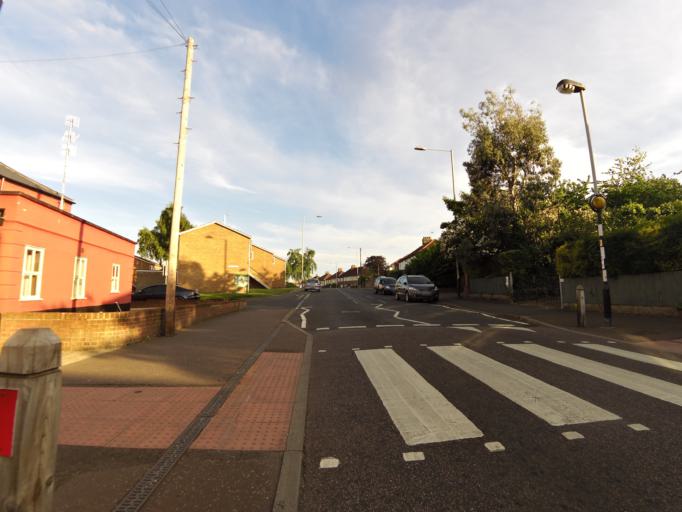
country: GB
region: England
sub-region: Norfolk
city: Norwich
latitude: 52.6451
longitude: 1.2913
